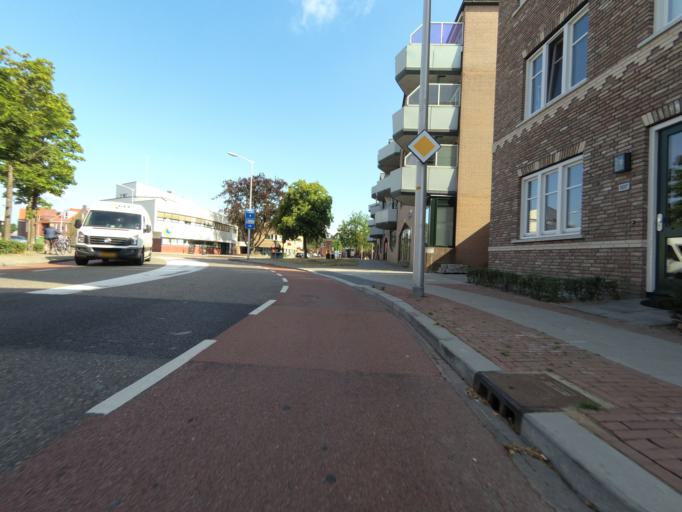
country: NL
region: Overijssel
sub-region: Gemeente Oldenzaal
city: Oldenzaal
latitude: 52.3095
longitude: 6.9273
